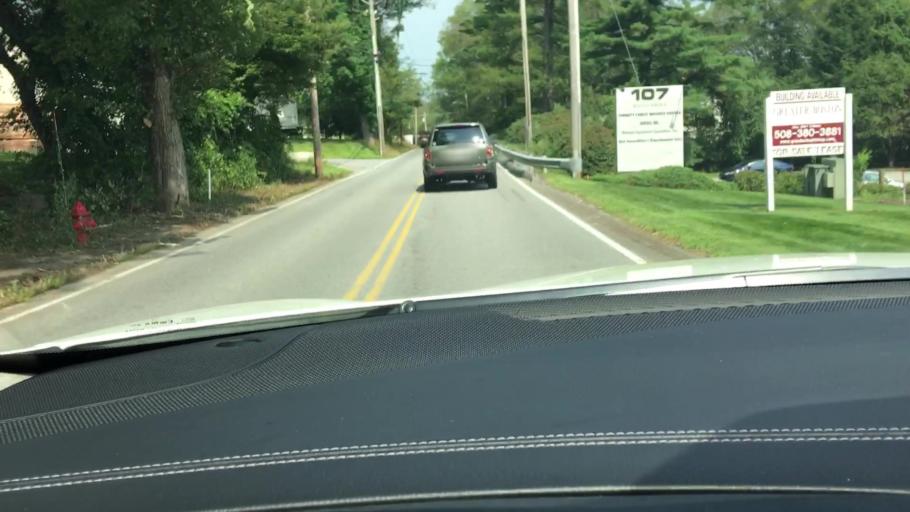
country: US
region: Massachusetts
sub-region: Worcester County
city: Northborough
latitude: 42.2902
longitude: -71.6562
